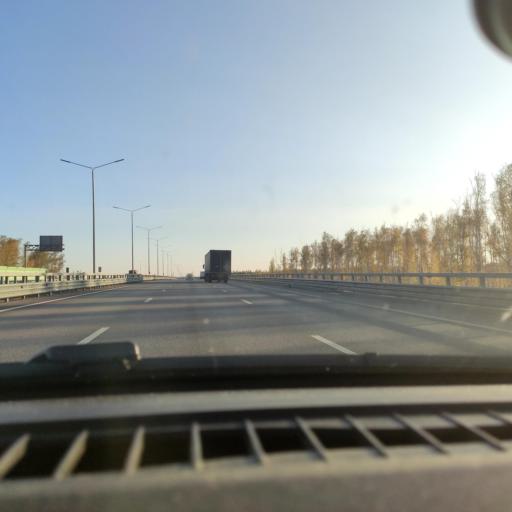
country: RU
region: Voronezj
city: Somovo
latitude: 51.7376
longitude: 39.3088
